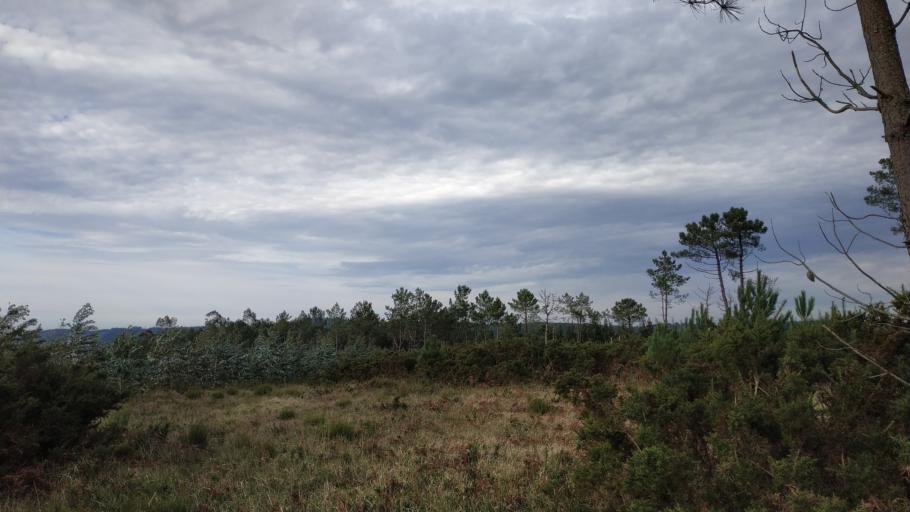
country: ES
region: Galicia
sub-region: Provincia de Pontevedra
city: Silleda
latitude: 42.7733
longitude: -8.1643
